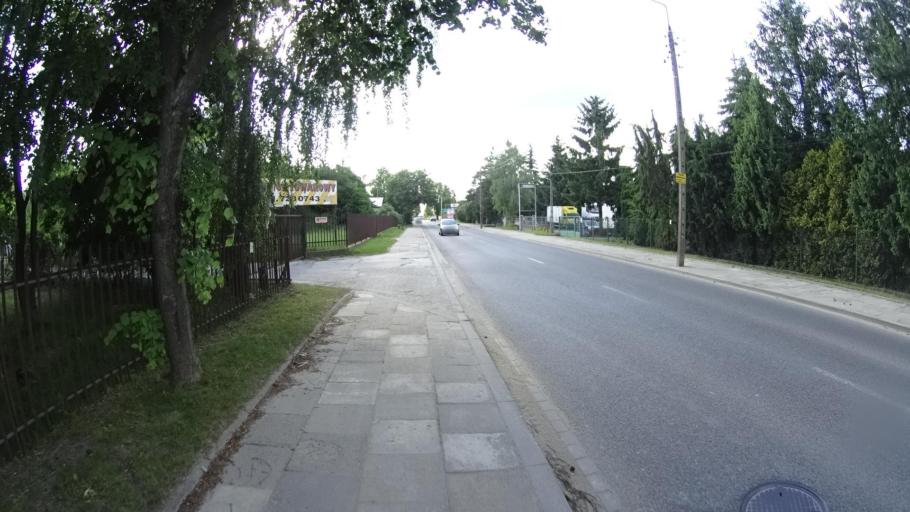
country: PL
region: Masovian Voivodeship
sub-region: Powiat pruszkowski
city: Pruszkow
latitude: 52.1740
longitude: 20.7749
